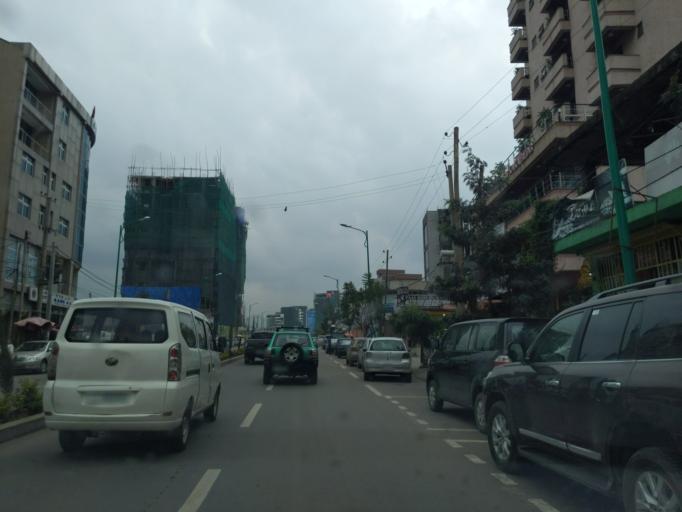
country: ET
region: Adis Abeba
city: Addis Ababa
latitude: 8.9955
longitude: 38.7667
